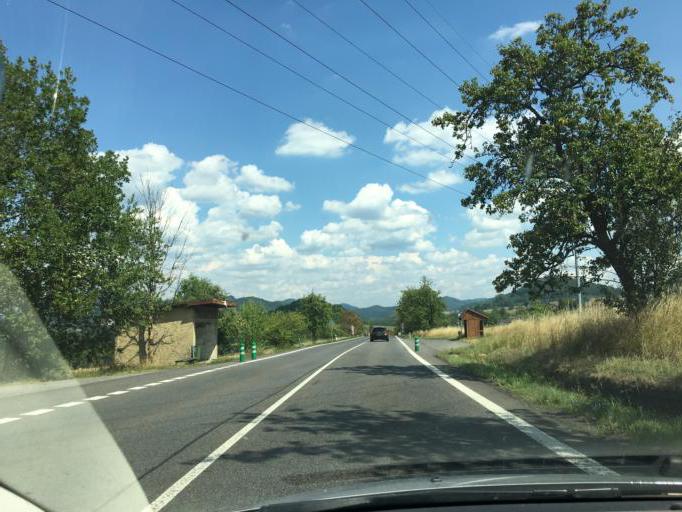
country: CZ
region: Ustecky
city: Ceska Kamenice
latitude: 50.7909
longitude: 14.3812
